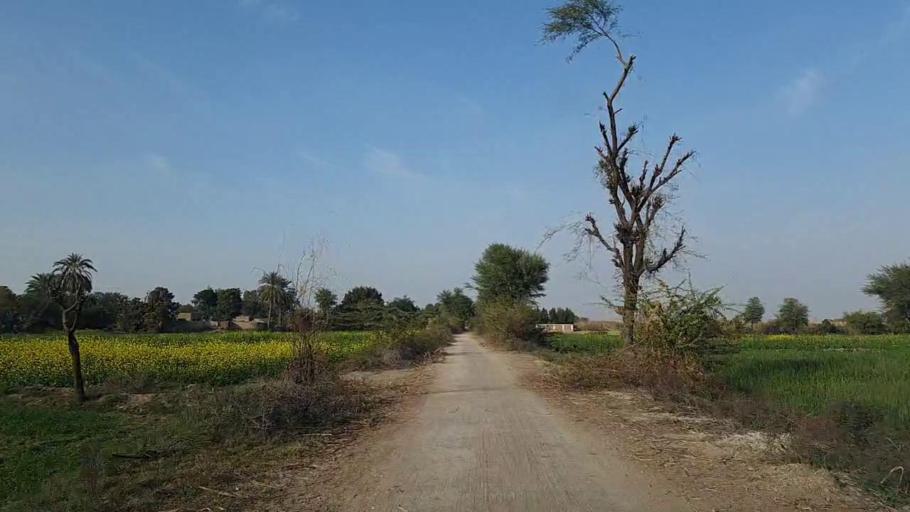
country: PK
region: Sindh
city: Nawabshah
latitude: 26.3807
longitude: 68.4850
